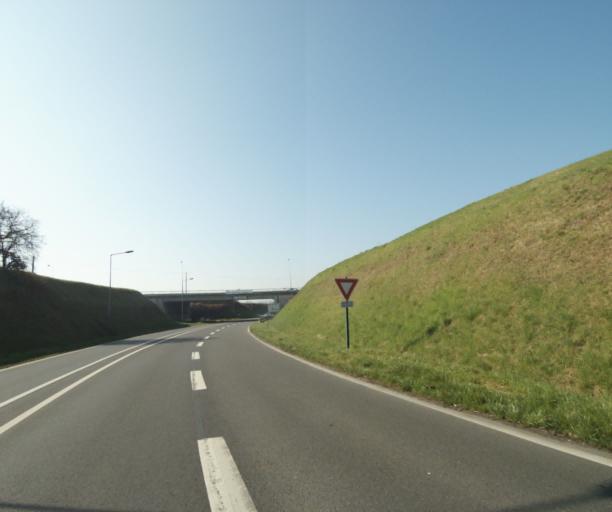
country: FR
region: Ile-de-France
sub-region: Departement du Val-d'Oise
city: Neuville-sur-Oise
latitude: 49.0245
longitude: 2.0603
